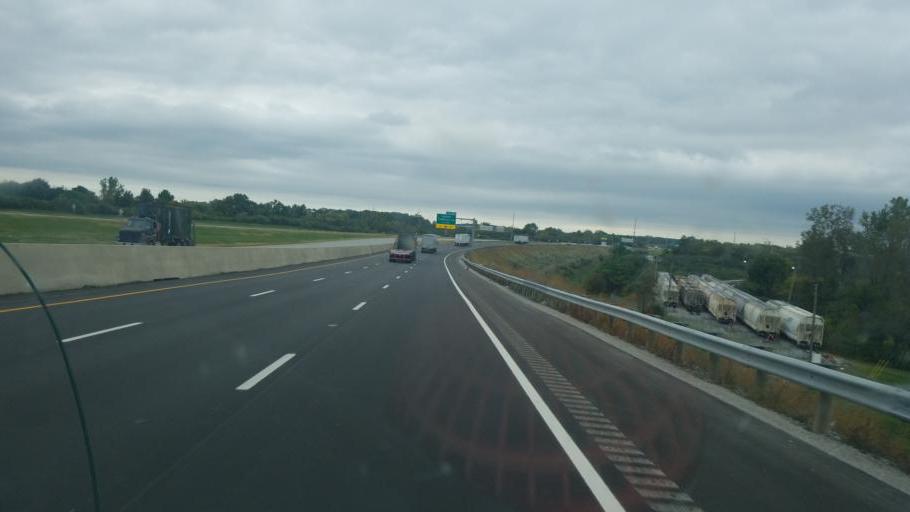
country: US
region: Ohio
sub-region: Lucas County
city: Waterville
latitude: 41.5312
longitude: -83.7141
